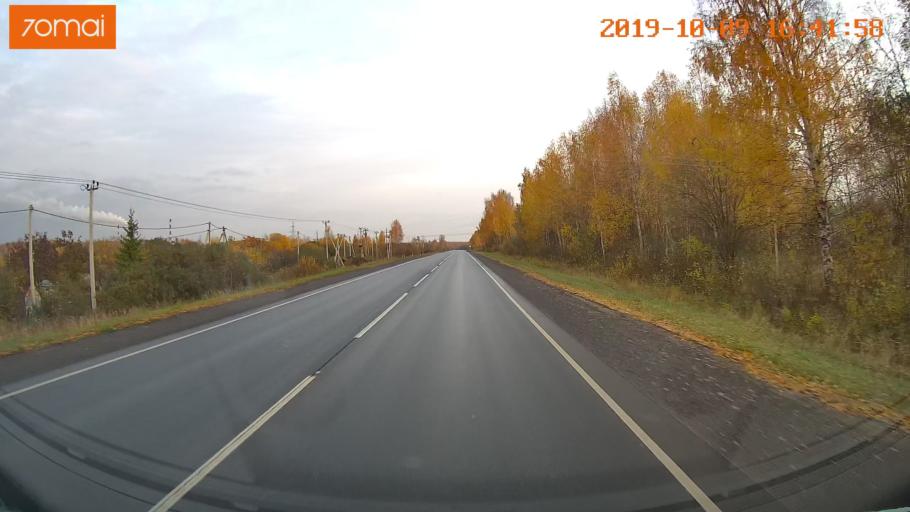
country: RU
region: Kostroma
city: Volgorechensk
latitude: 57.4674
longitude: 41.0911
